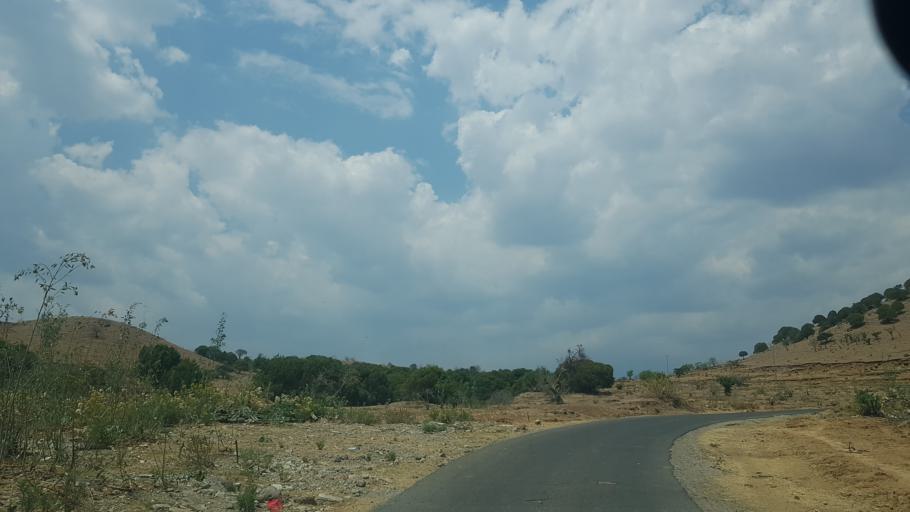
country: MX
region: Puebla
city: San Juan Amecac
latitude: 18.8114
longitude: -98.6245
